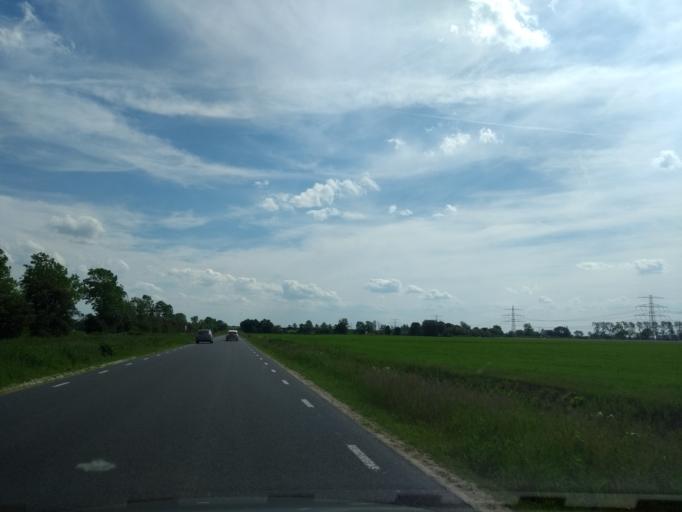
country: NL
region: Groningen
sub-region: Gemeente Zuidhorn
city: Aduard
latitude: 53.2518
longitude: 6.4805
